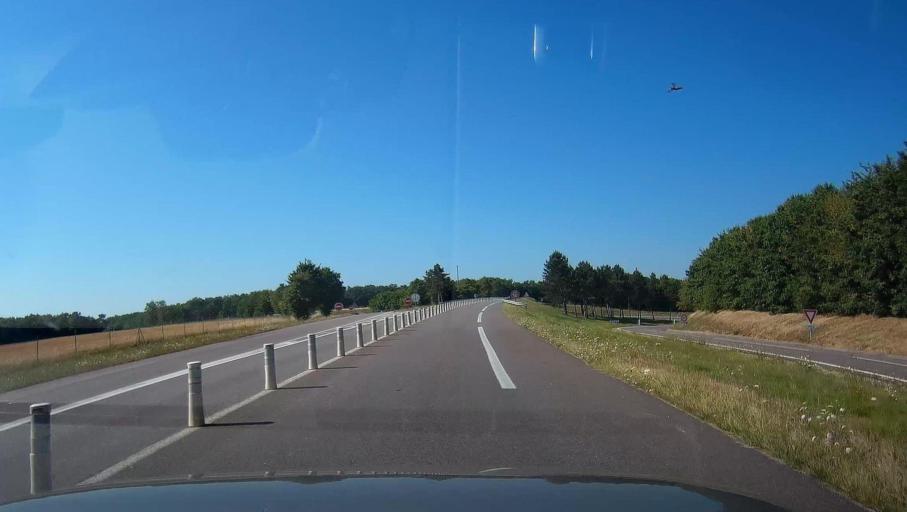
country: FR
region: Lorraine
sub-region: Departement de Meurthe-et-Moselle
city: Colombey-les-Belles
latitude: 48.5383
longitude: 5.9076
